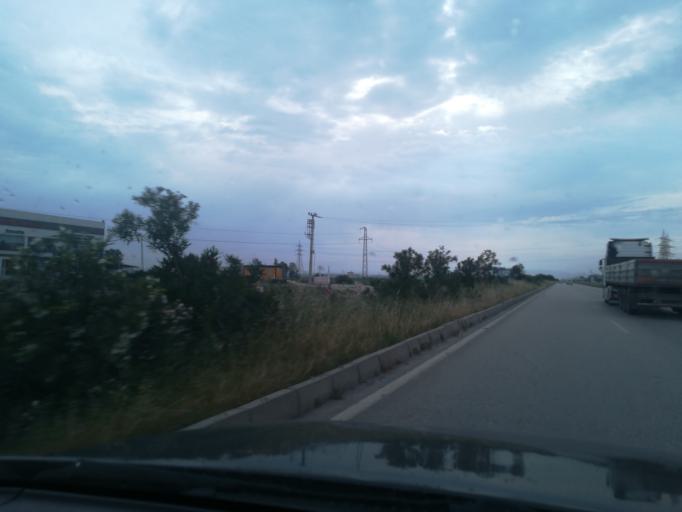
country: TR
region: Adana
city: Yuregir
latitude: 36.9800
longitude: 35.4509
